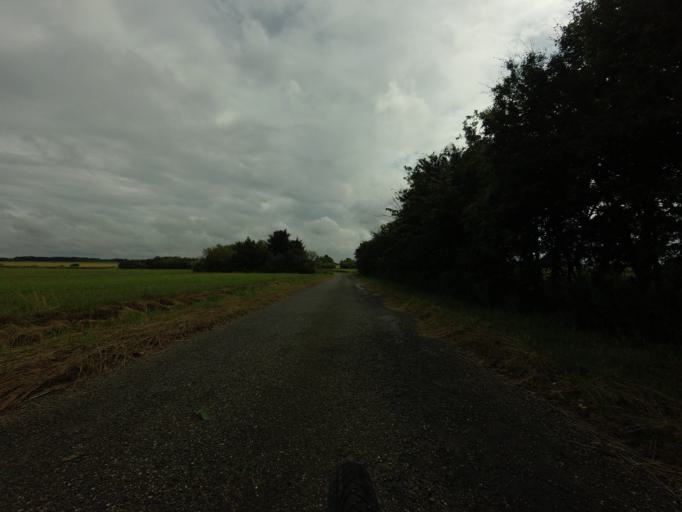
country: DK
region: North Denmark
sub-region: Jammerbugt Kommune
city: Pandrup
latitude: 57.3133
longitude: 9.7415
